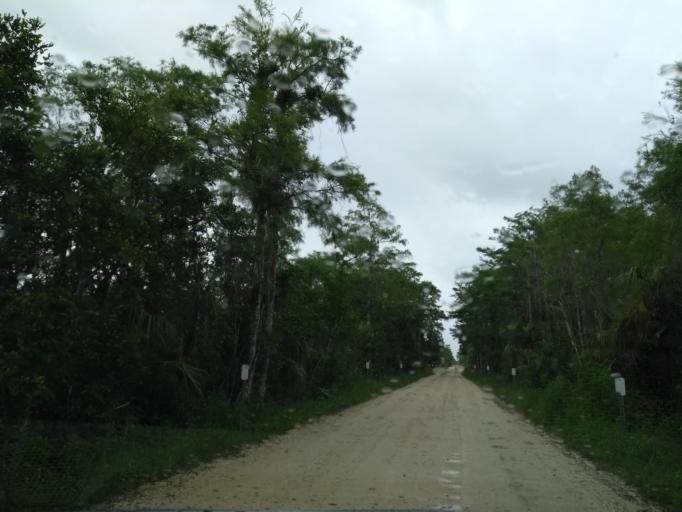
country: US
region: Florida
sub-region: Miami-Dade County
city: The Hammocks
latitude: 25.7604
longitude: -81.0079
